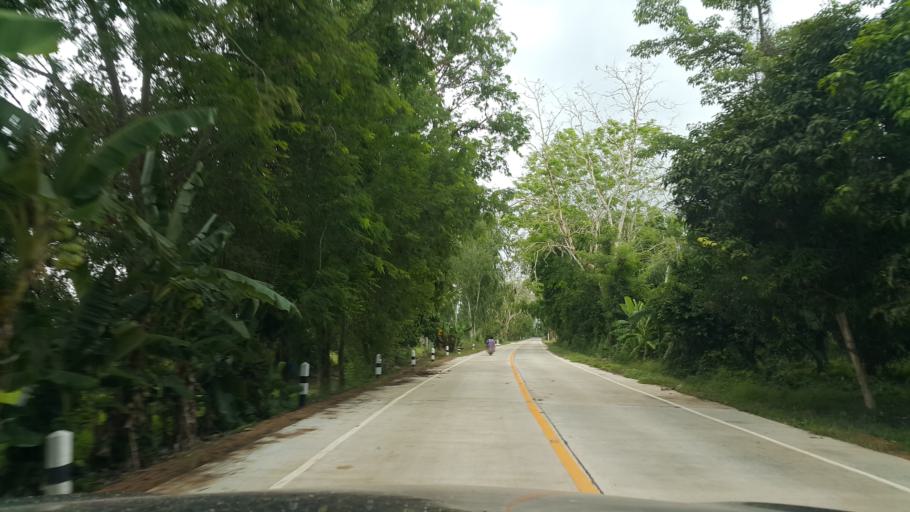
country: TH
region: Sukhothai
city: Kong Krailat
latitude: 16.9251
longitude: 99.8957
